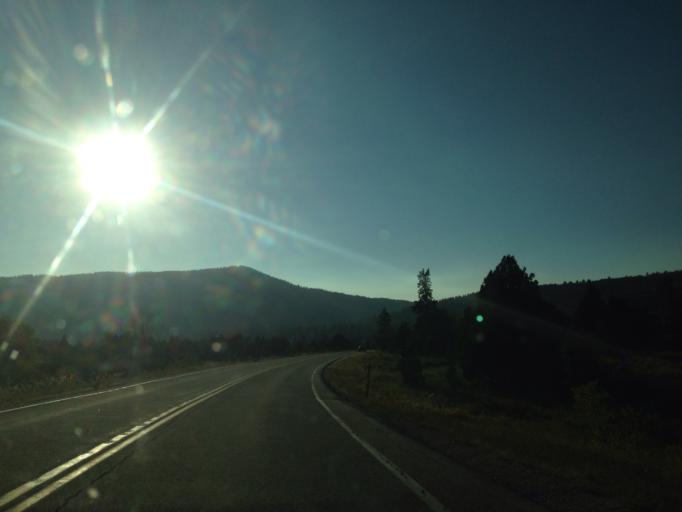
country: US
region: Utah
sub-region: Summit County
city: Francis
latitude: 40.5944
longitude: -111.0888
